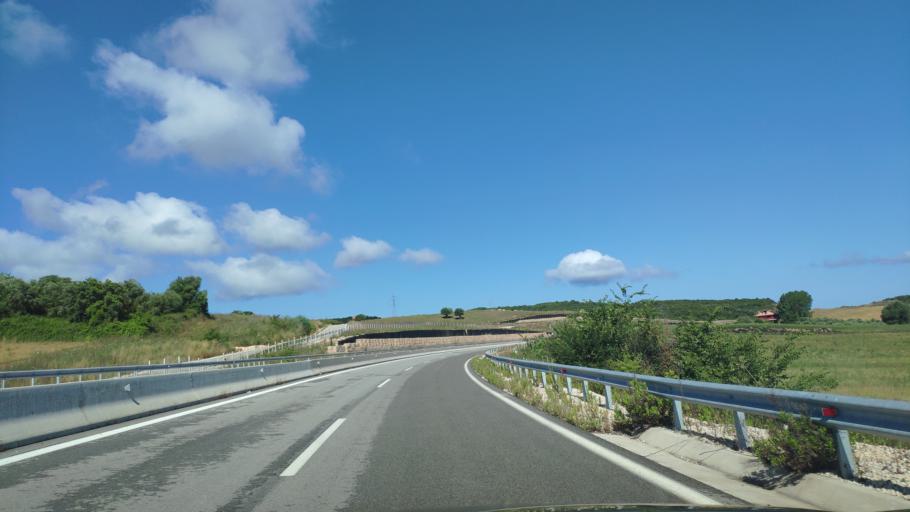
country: GR
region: West Greece
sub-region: Nomos Aitolias kai Akarnanias
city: Vonitsa
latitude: 38.9102
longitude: 20.8349
